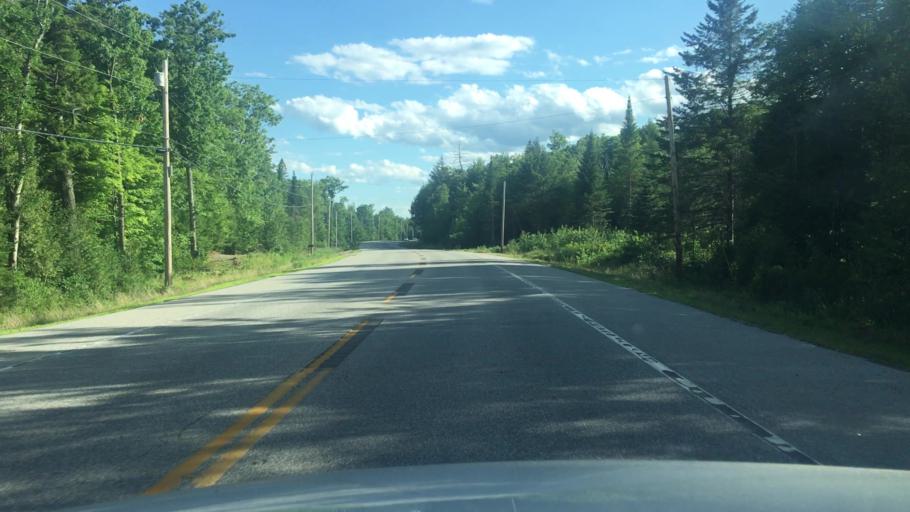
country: US
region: Maine
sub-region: Androscoggin County
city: Livermore
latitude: 44.4032
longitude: -70.2265
